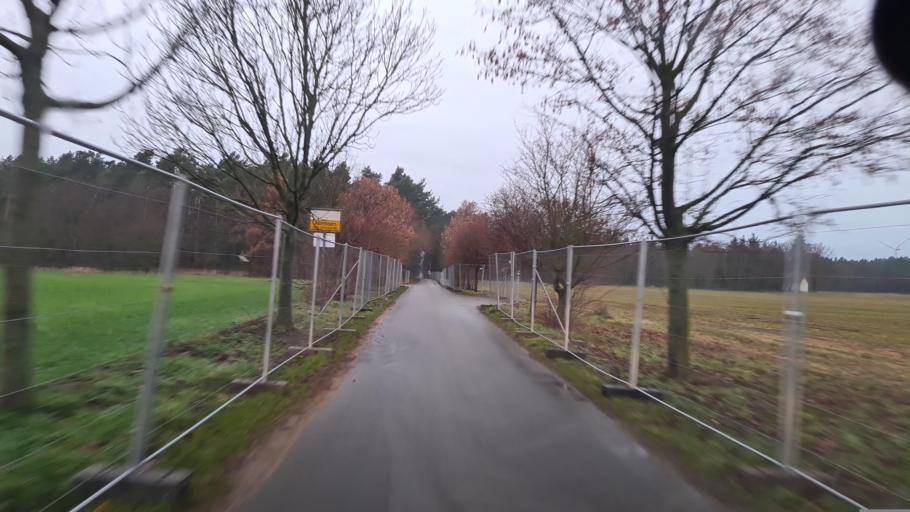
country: DE
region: Brandenburg
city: Grossraschen
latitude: 51.5813
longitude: 14.0884
